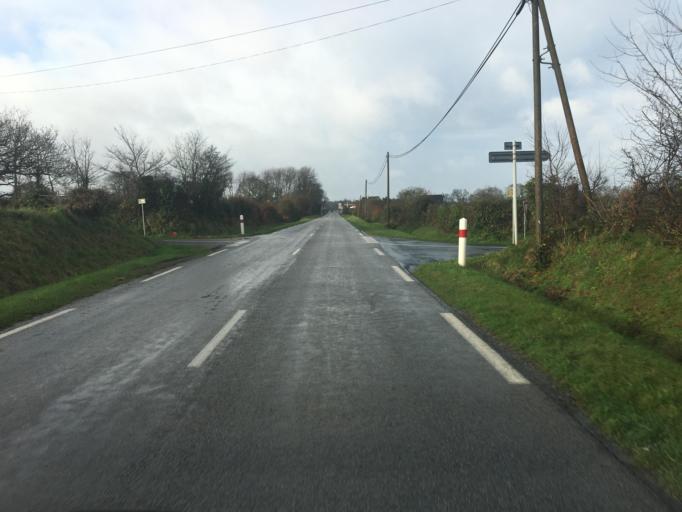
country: FR
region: Lower Normandy
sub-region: Departement de la Manche
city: Saint-Pierre-Eglise
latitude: 49.6676
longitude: -1.3865
